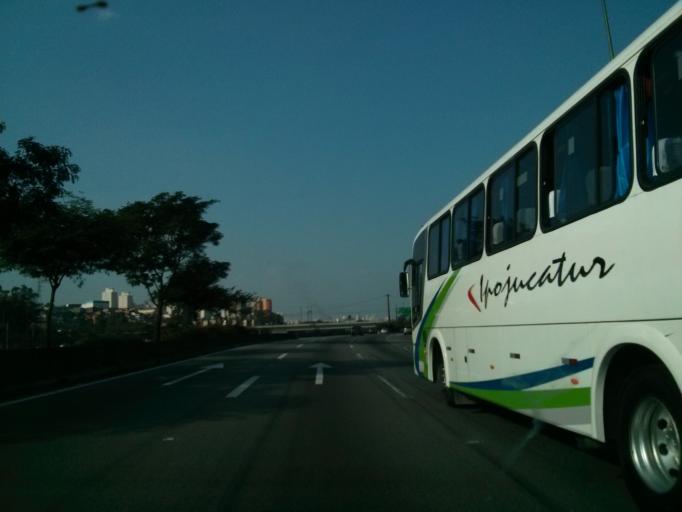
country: BR
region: Sao Paulo
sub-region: Osasco
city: Osasco
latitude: -23.5088
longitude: -46.7179
